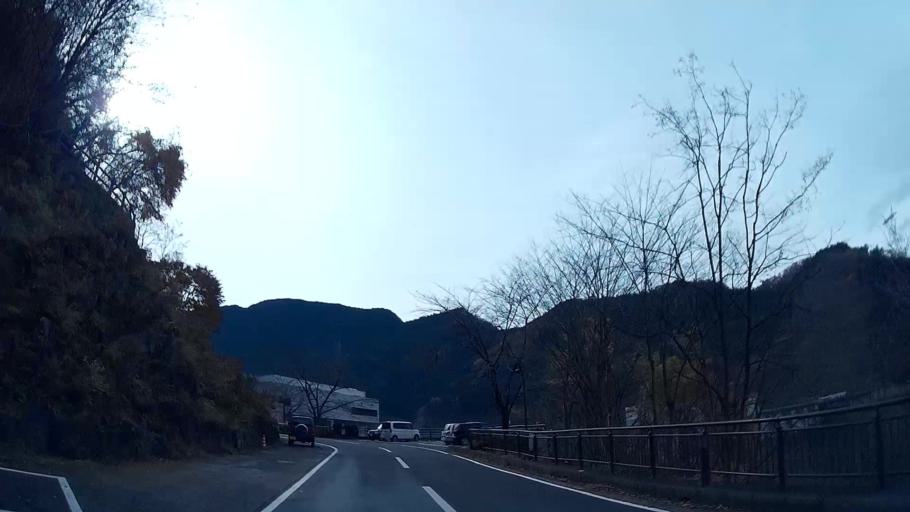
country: JP
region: Saitama
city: Chichibu
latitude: 35.9539
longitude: 139.0551
